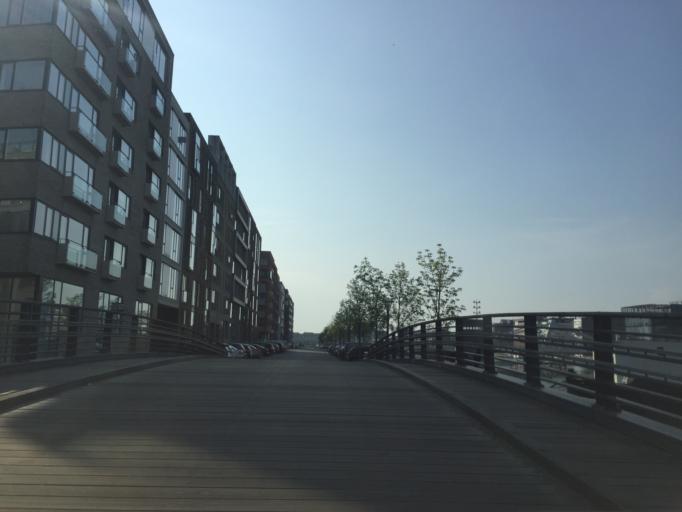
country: DK
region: Capital Region
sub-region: Kobenhavn
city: Copenhagen
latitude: 55.6466
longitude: 12.5520
